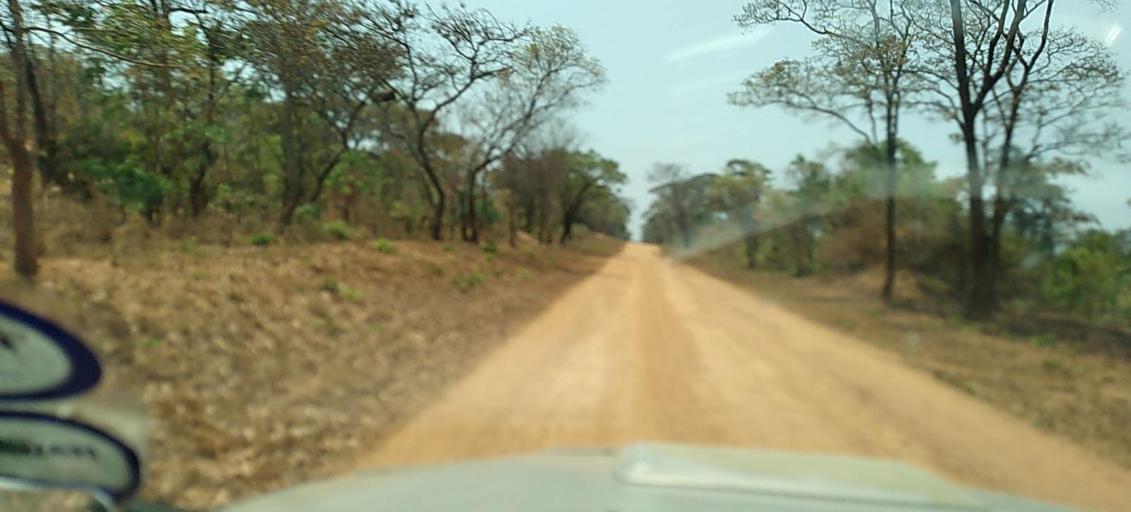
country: ZM
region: North-Western
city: Kasempa
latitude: -13.5488
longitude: 26.0315
